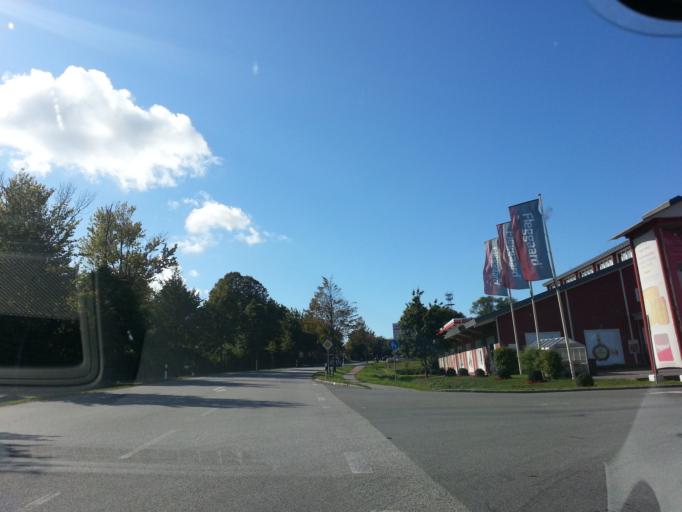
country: DE
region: Schleswig-Holstein
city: Heiligenhafen
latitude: 54.3652
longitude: 11.0043
